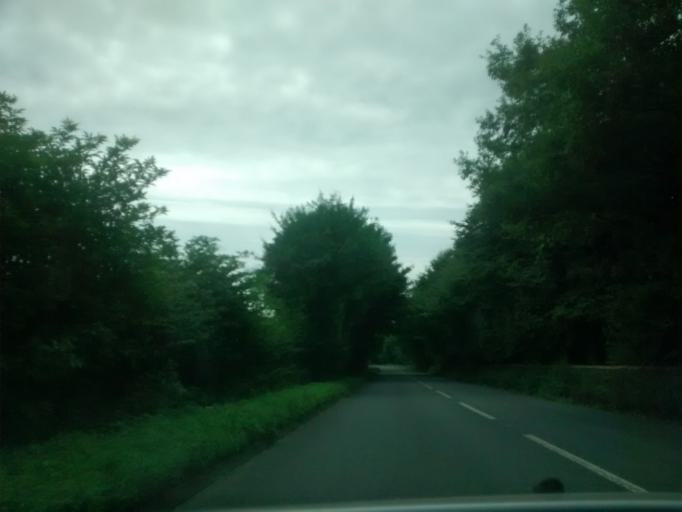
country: GB
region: England
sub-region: South Gloucestershire
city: Horton
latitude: 51.5138
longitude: -2.3436
